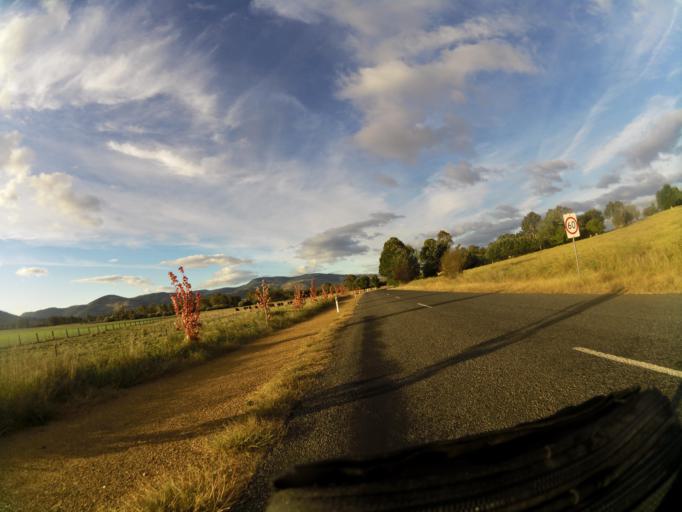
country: AU
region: New South Wales
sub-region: Greater Hume Shire
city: Holbrook
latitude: -36.0481
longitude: 147.9253
